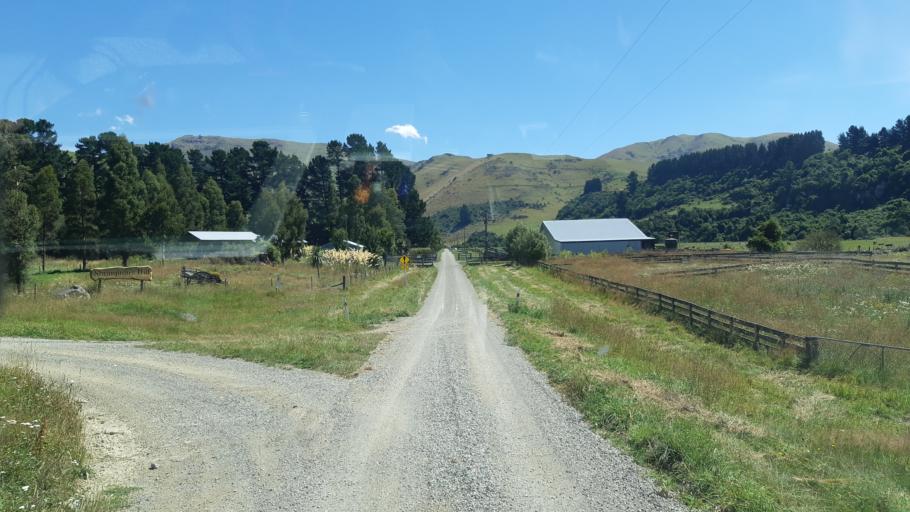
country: NZ
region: Canterbury
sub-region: Timaru District
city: Pleasant Point
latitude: -44.3335
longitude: 170.8685
